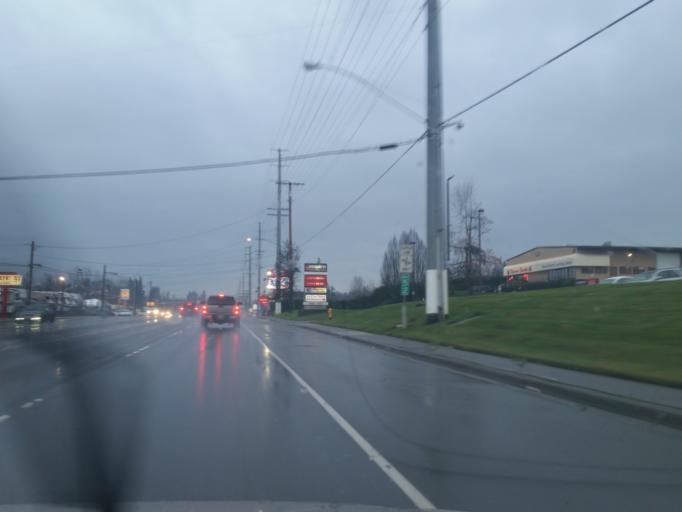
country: US
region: Washington
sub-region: Snohomish County
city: Martha Lake
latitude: 47.8853
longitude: -122.2625
